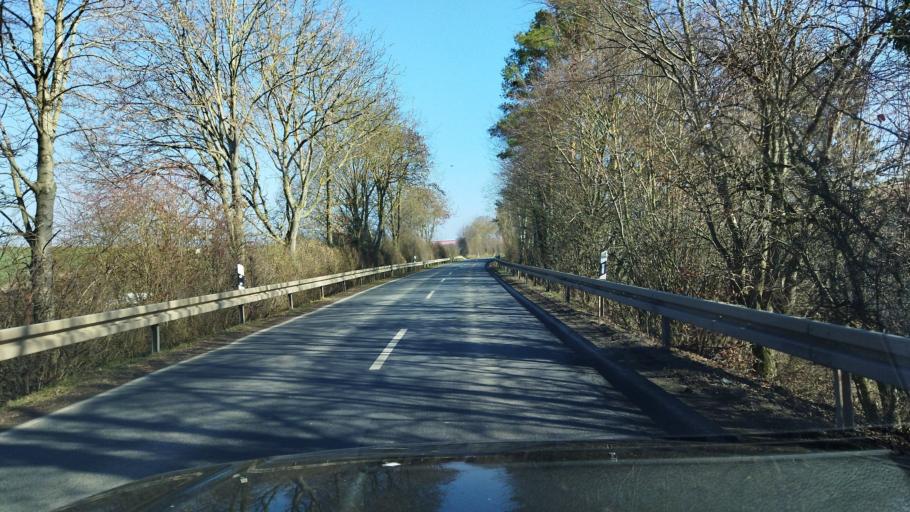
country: DE
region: Bavaria
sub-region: Regierungsbezirk Unterfranken
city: Buchbrunn
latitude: 49.7619
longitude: 10.1354
